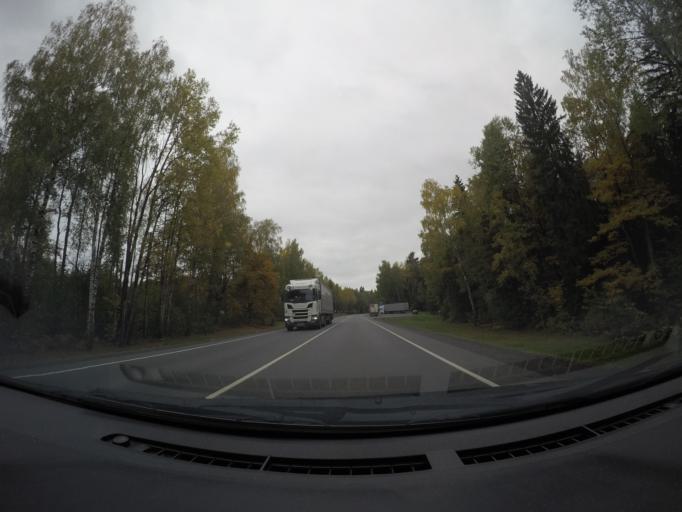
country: RU
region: Moskovskaya
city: Ruza
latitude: 55.7535
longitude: 36.2583
